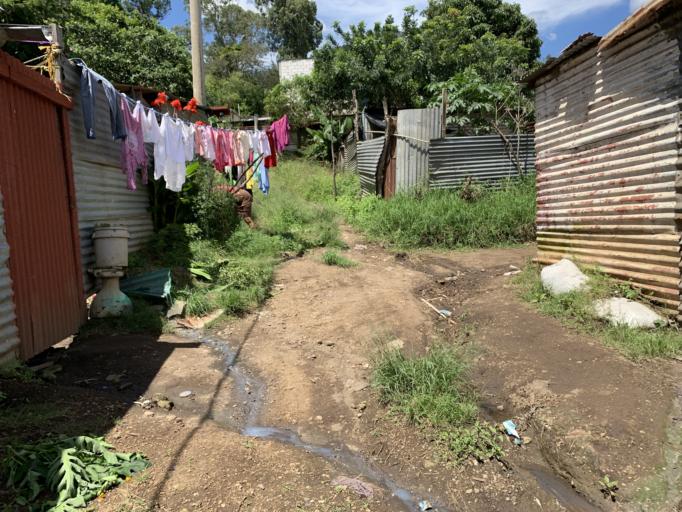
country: GT
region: Guatemala
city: Amatitlan
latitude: 14.4860
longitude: -90.6428
